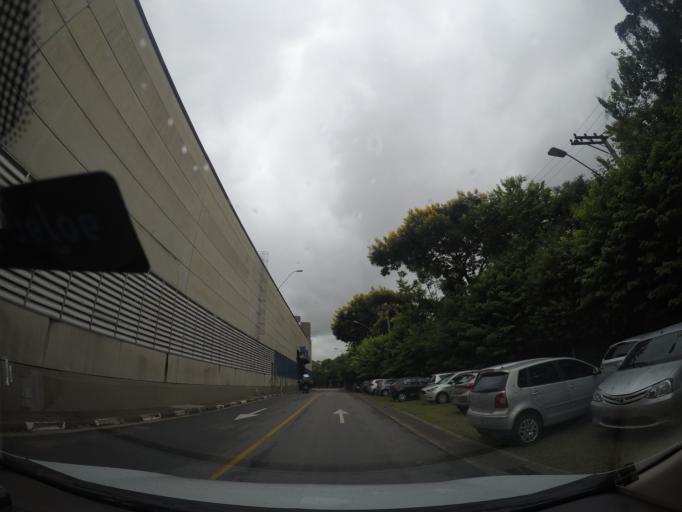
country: BR
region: Sao Paulo
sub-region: Osasco
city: Osasco
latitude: -23.4987
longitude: -46.7572
